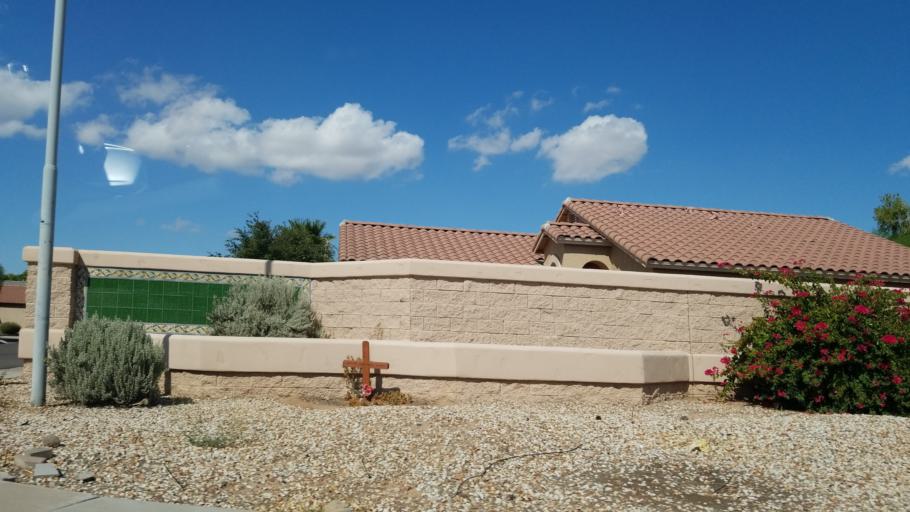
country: US
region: Arizona
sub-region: Maricopa County
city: Tolleson
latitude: 33.4825
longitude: -112.2379
